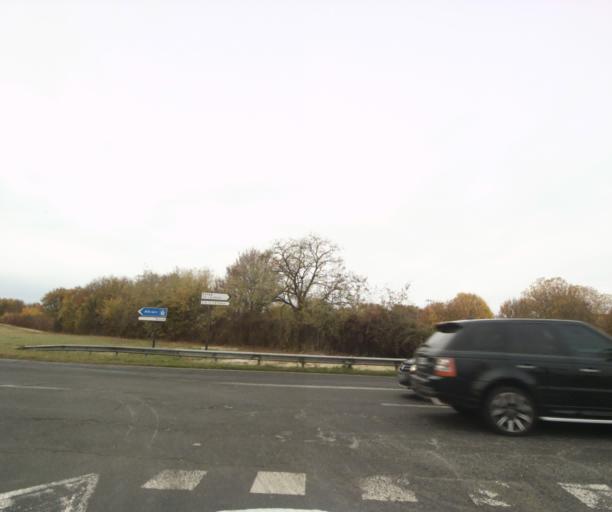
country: FR
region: Poitou-Charentes
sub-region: Departement de la Charente-Maritime
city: Saintes
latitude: 45.7454
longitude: -0.6697
